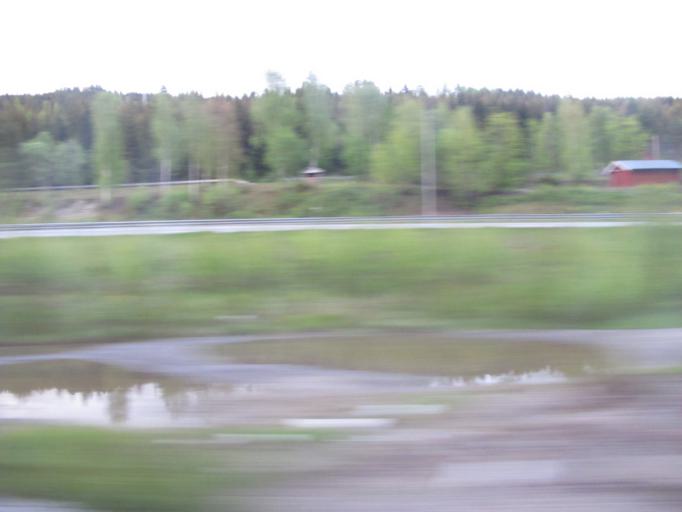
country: NO
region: Oppland
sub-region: Lillehammer
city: Lillehammer
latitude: 61.2108
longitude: 10.4352
